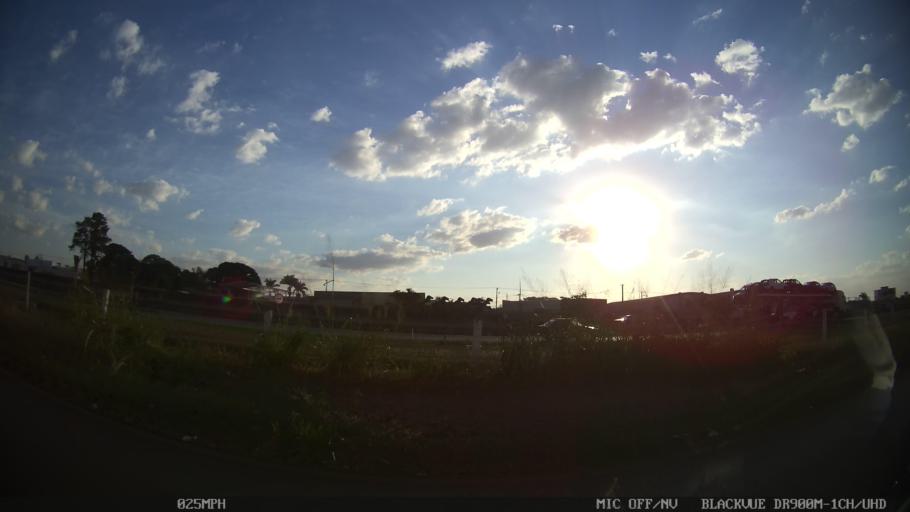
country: BR
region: Sao Paulo
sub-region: Ribeirao Preto
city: Ribeirao Preto
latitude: -21.1825
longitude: -47.7567
